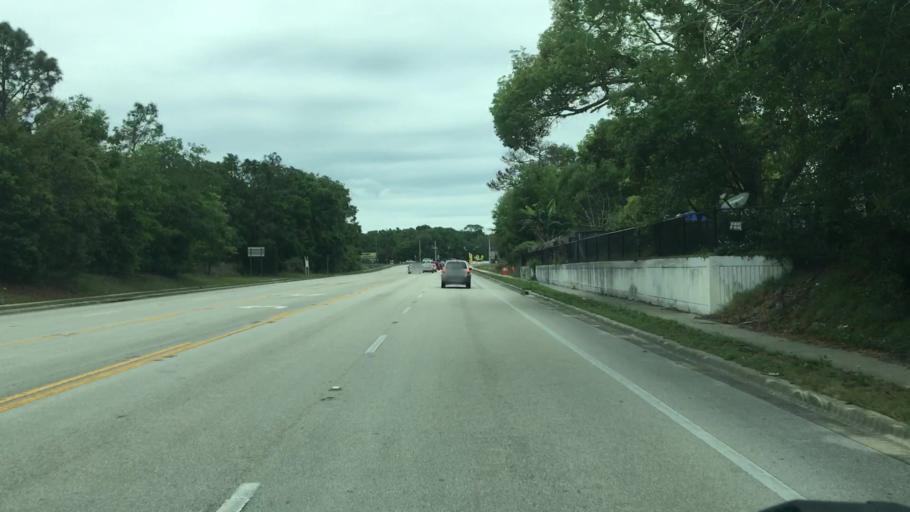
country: US
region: Florida
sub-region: Volusia County
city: De Land Southwest
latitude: 29.0107
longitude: -81.3212
